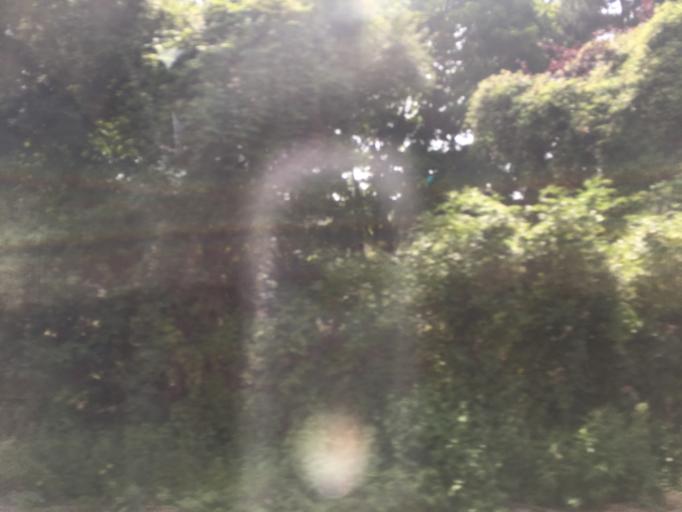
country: DE
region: Hesse
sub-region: Regierungsbezirk Darmstadt
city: Eschborn
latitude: 50.1387
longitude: 8.5999
